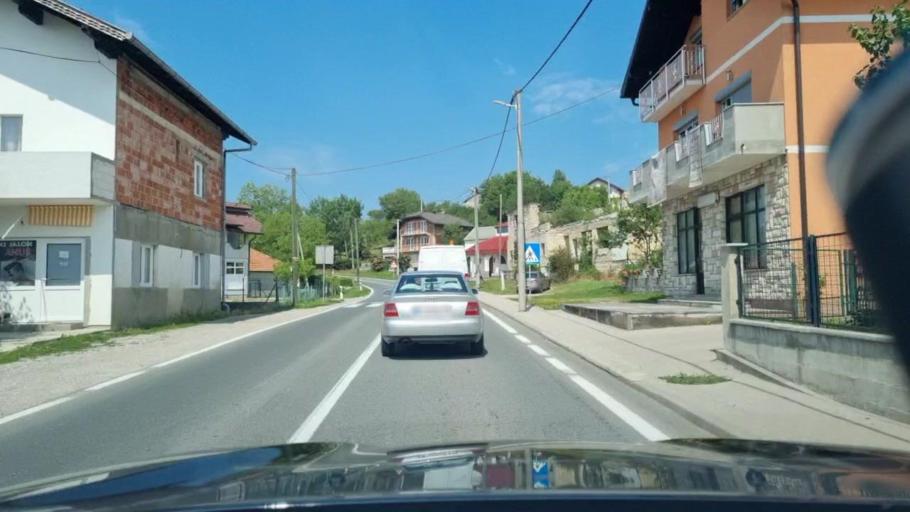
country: BA
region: Federation of Bosnia and Herzegovina
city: Izacic
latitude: 44.8749
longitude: 15.7821
